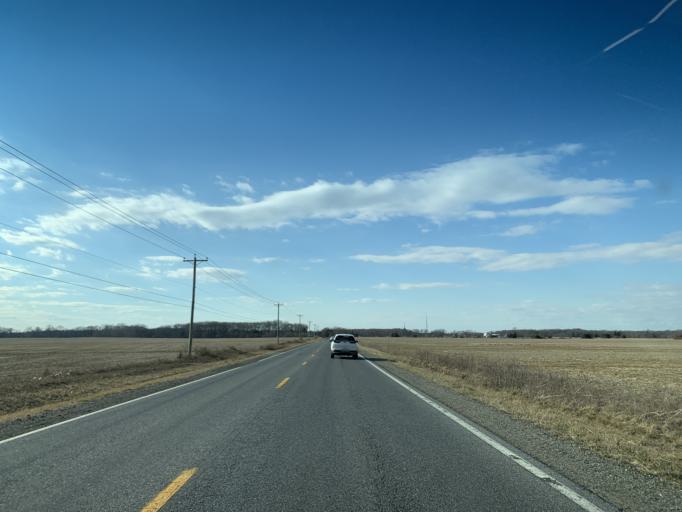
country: US
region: Maryland
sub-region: Queen Anne's County
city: Centreville
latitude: 39.0152
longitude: -76.0006
